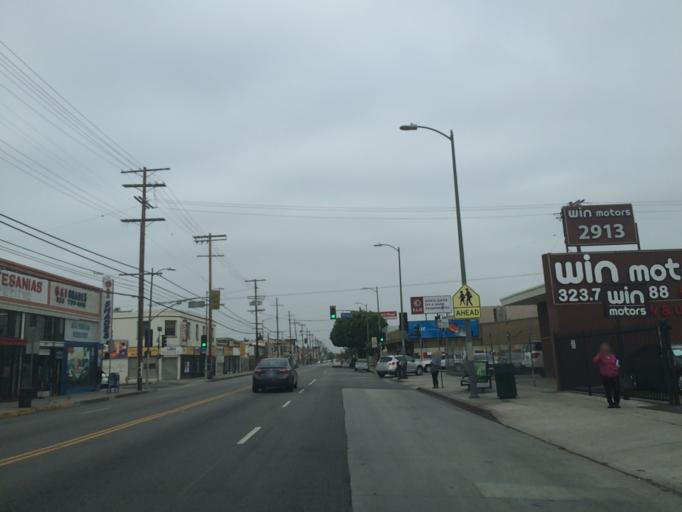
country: US
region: California
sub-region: Los Angeles County
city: Silver Lake
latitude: 34.0472
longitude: -118.3035
